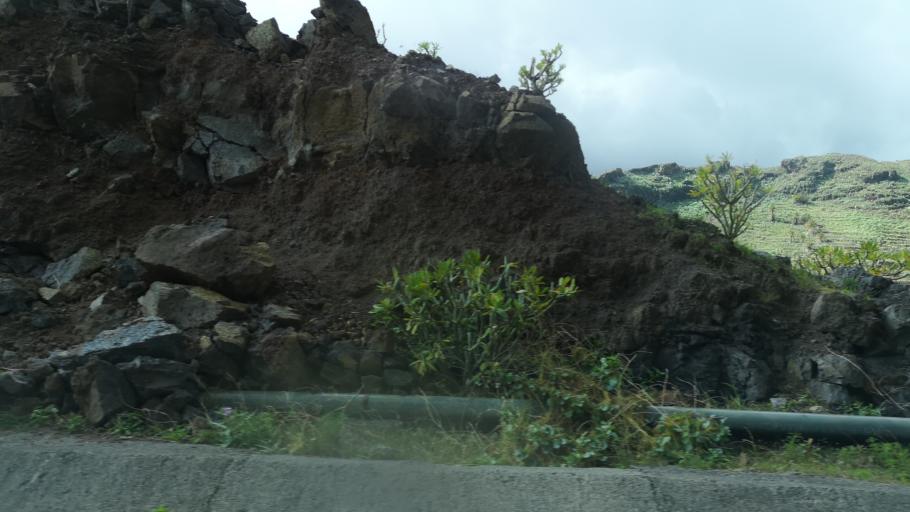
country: ES
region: Canary Islands
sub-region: Provincia de Santa Cruz de Tenerife
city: San Sebastian de la Gomera
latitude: 28.1176
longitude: -17.1418
